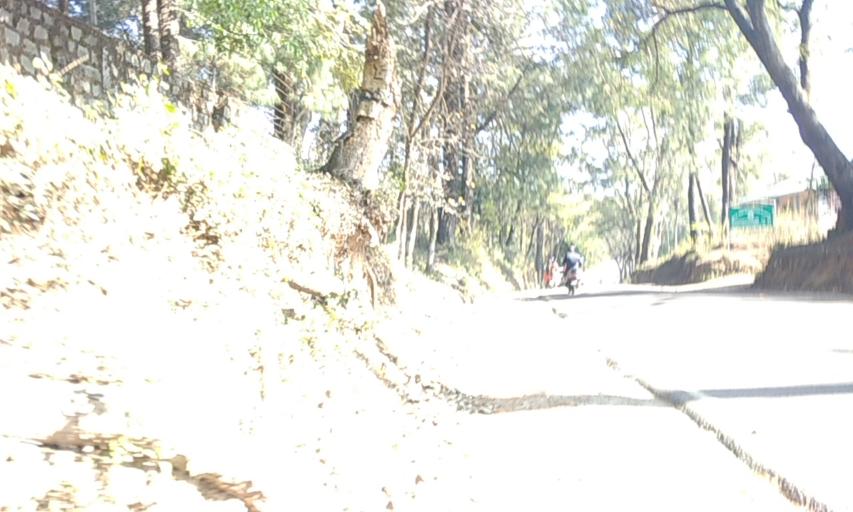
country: IN
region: Himachal Pradesh
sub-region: Kangra
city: Palampur
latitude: 32.1046
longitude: 76.5533
